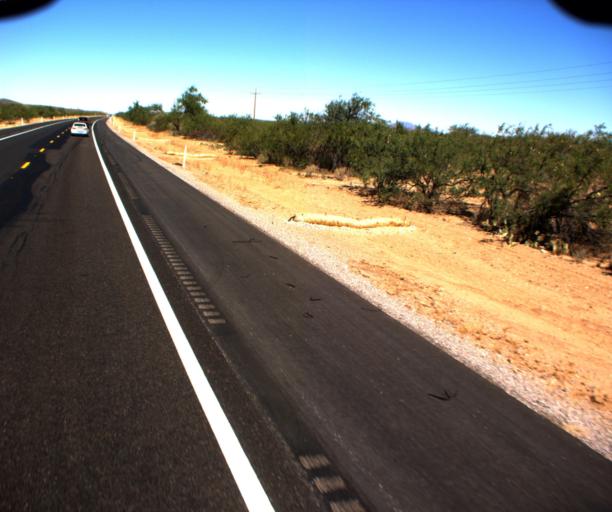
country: US
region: Arizona
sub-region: Pima County
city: Sells
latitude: 31.9200
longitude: -111.8278
